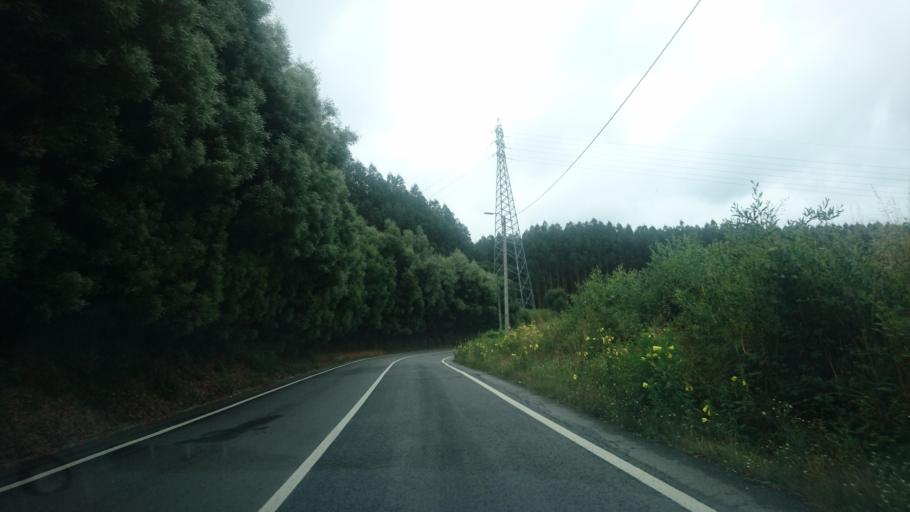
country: PT
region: Aveiro
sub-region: Santa Maria da Feira
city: Sao Joao de Ver
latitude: 40.9599
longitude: -8.5461
